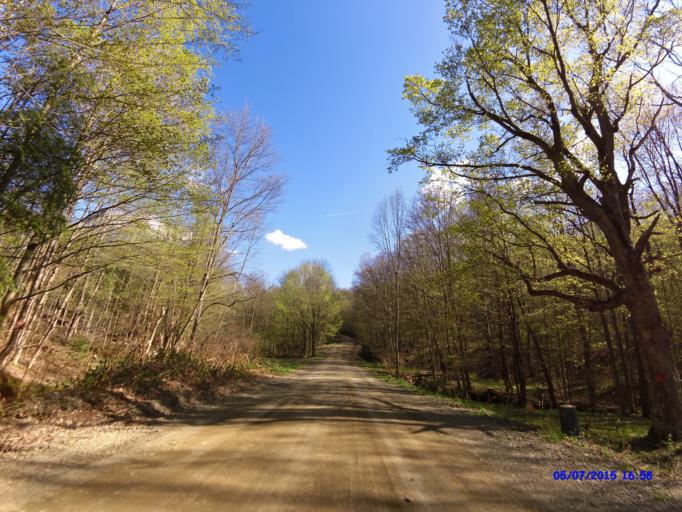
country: US
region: New York
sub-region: Cattaraugus County
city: Little Valley
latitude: 42.2943
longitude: -78.7467
